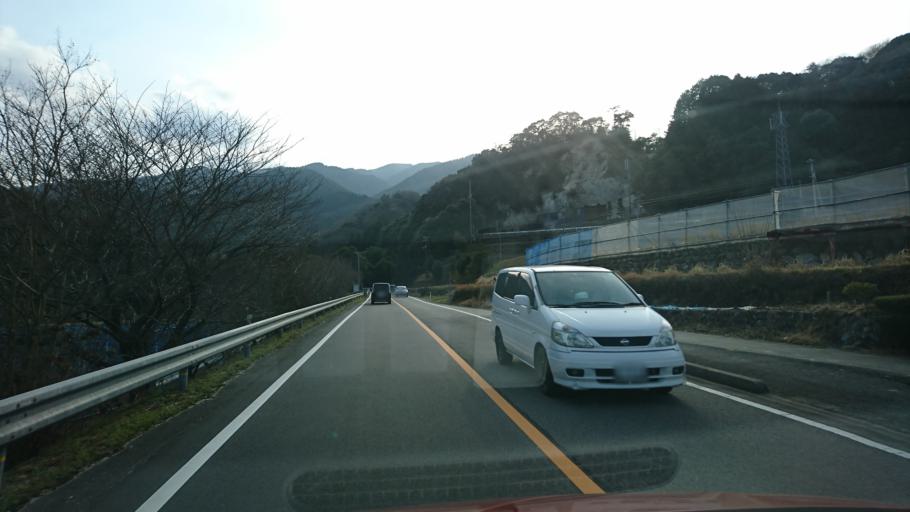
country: JP
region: Ehime
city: Hojo
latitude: 33.9752
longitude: 132.9036
